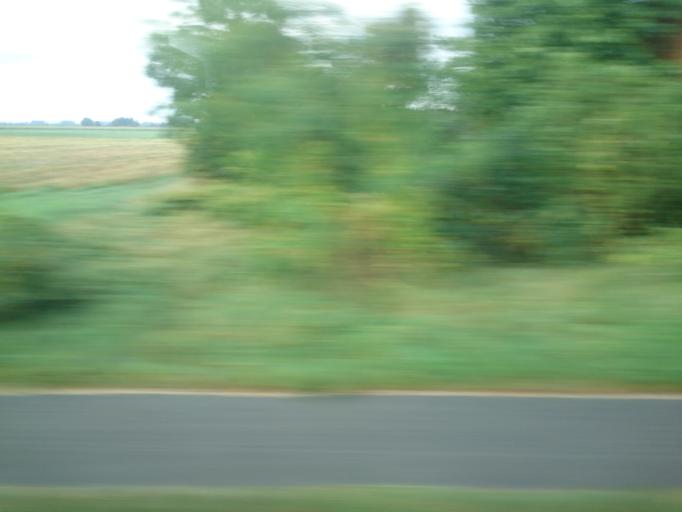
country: DE
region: Mecklenburg-Vorpommern
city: Ferdinandshof
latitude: 53.7018
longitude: 13.8604
